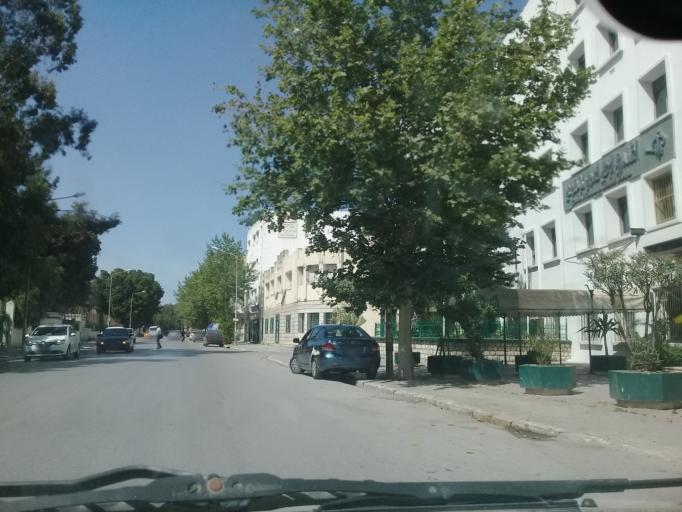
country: TN
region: Tunis
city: Tunis
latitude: 36.8143
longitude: 10.1754
